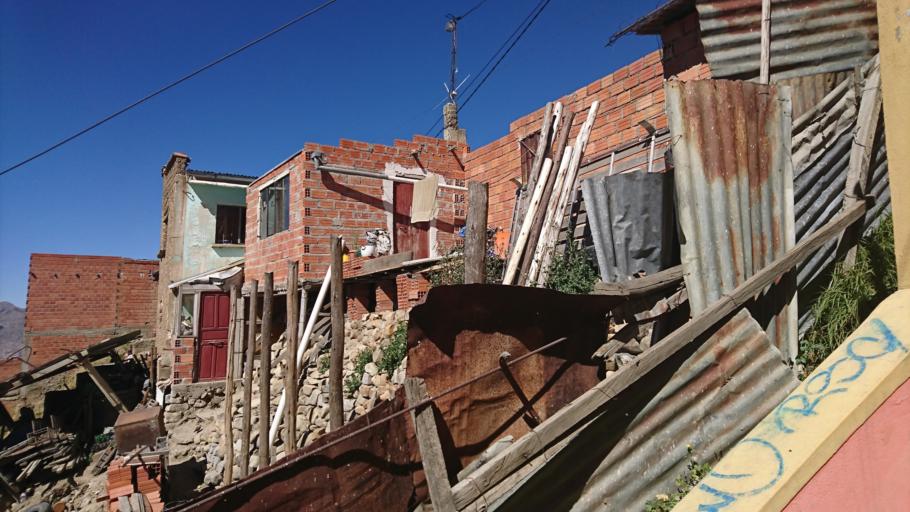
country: BO
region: La Paz
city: La Paz
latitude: -16.4923
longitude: -68.1025
